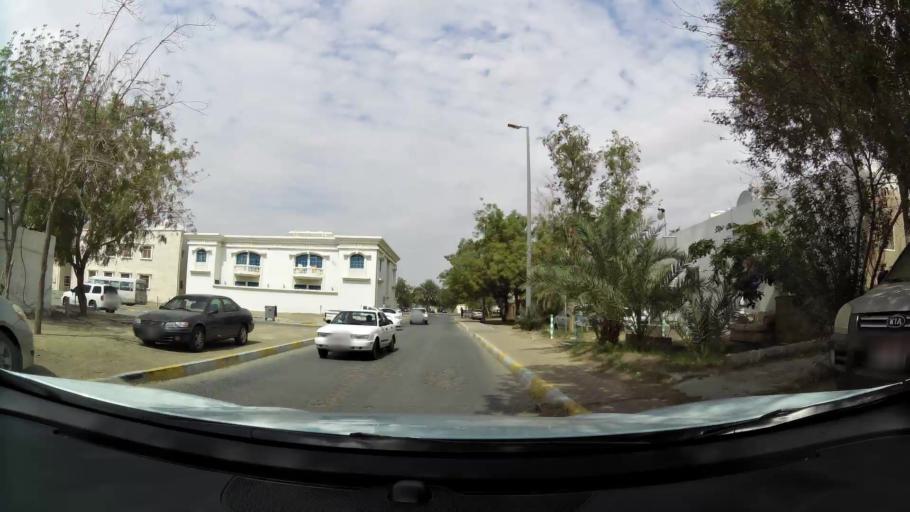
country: AE
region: Abu Dhabi
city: Al Ain
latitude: 24.2134
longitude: 55.7842
